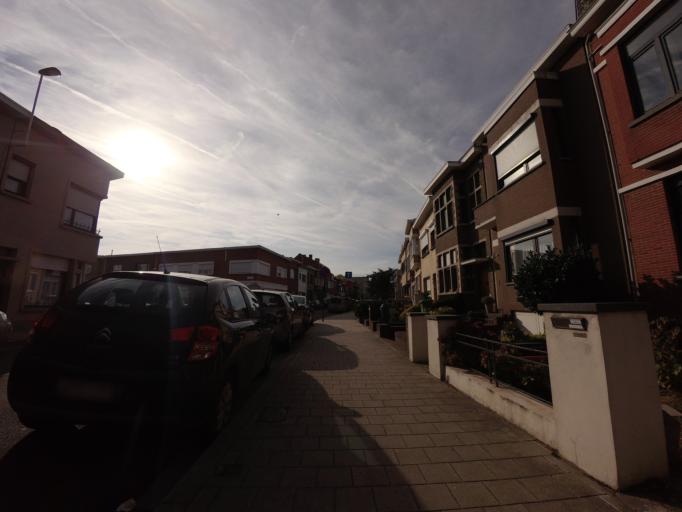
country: BE
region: Flanders
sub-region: Provincie Antwerpen
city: Borsbeek
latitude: 51.2271
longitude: 4.4709
